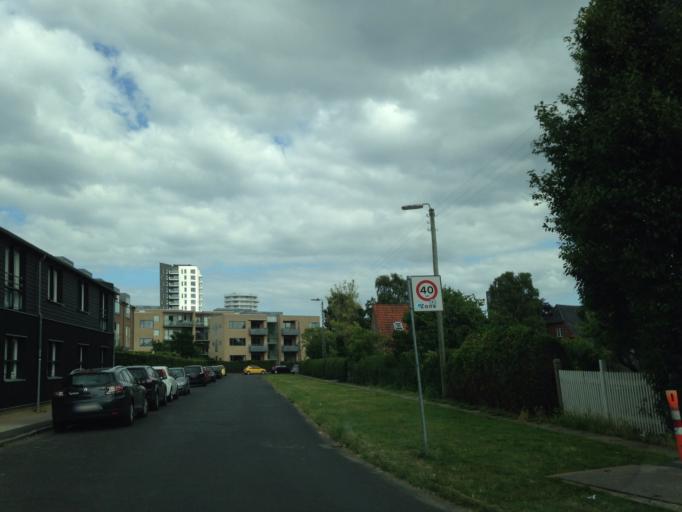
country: DK
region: Capital Region
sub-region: Kobenhavn
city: Christianshavn
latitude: 55.6604
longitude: 12.6257
